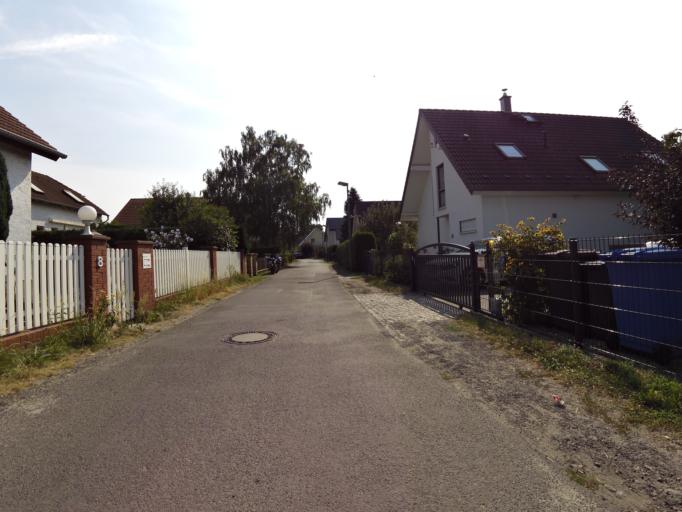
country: DE
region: Berlin
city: Adlershof
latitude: 52.4231
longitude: 13.5460
